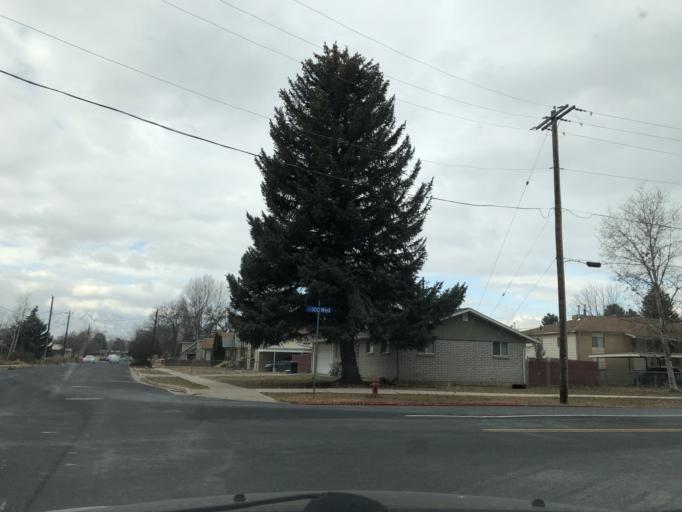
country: US
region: Utah
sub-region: Cache County
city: Logan
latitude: 41.7208
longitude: -111.8378
